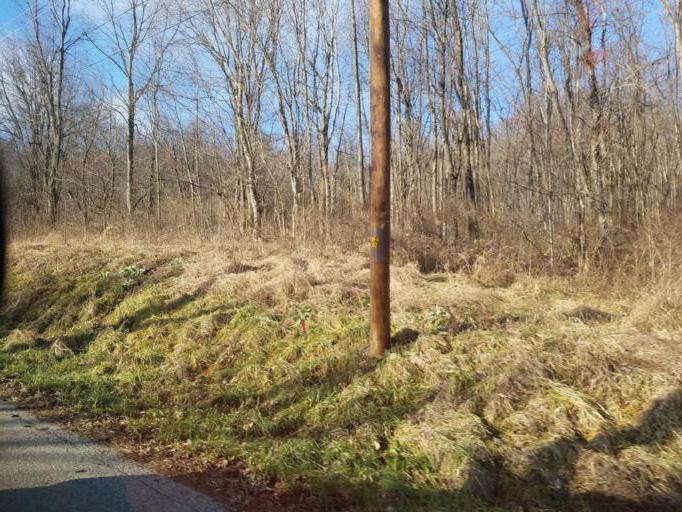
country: US
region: Ohio
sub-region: Sandusky County
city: Bellville
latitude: 40.5800
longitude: -82.4546
